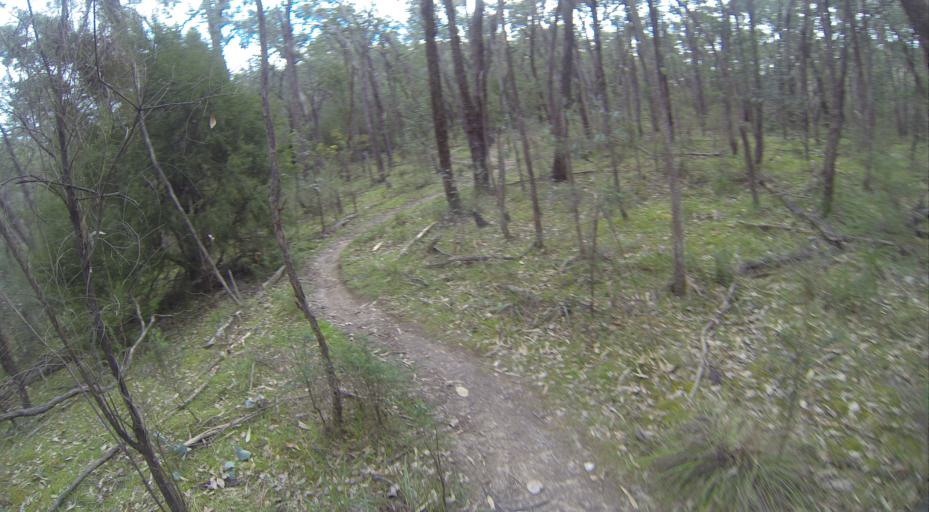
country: AU
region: Victoria
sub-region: Nillumbik
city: Saint Andrews
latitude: -37.6395
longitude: 145.2960
